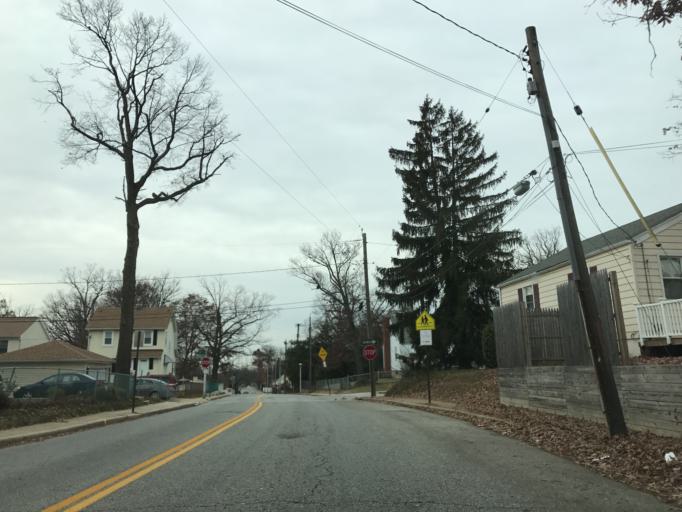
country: US
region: Maryland
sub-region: Baltimore County
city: Parkville
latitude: 39.3659
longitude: -76.5404
